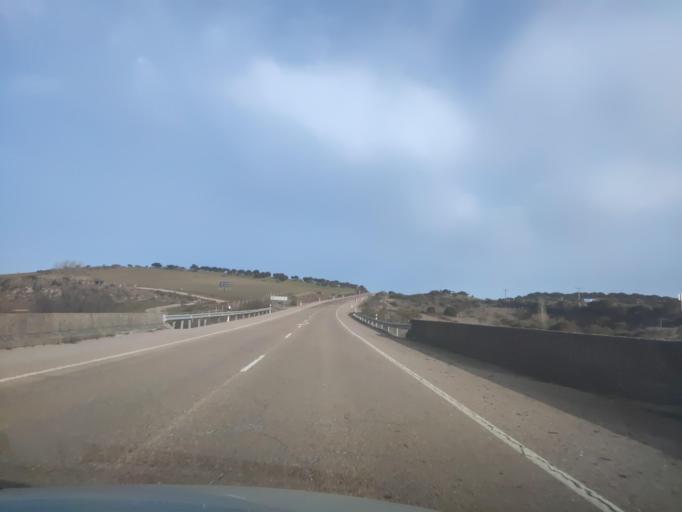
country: ES
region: Castille and Leon
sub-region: Provincia de Salamanca
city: Carpio de Azaba
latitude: 40.5909
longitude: -6.6693
